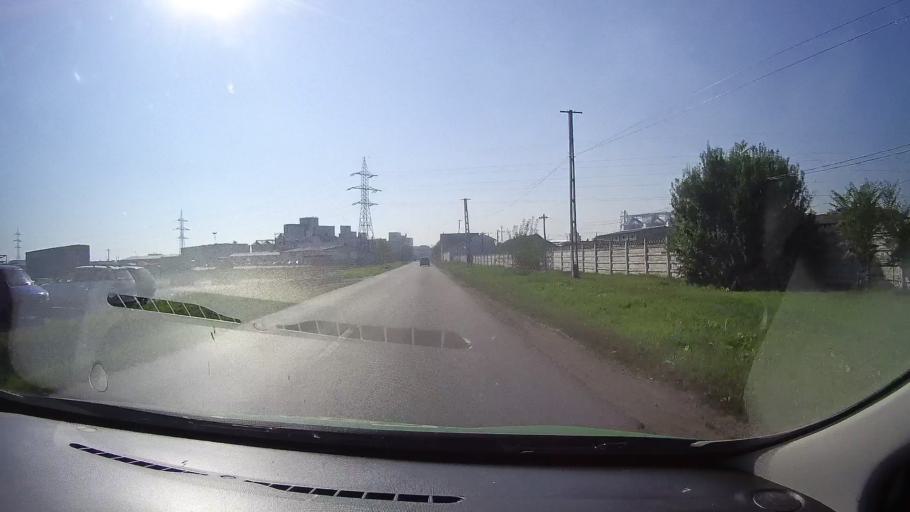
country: RO
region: Satu Mare
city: Carei
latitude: 47.7020
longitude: 22.4660
